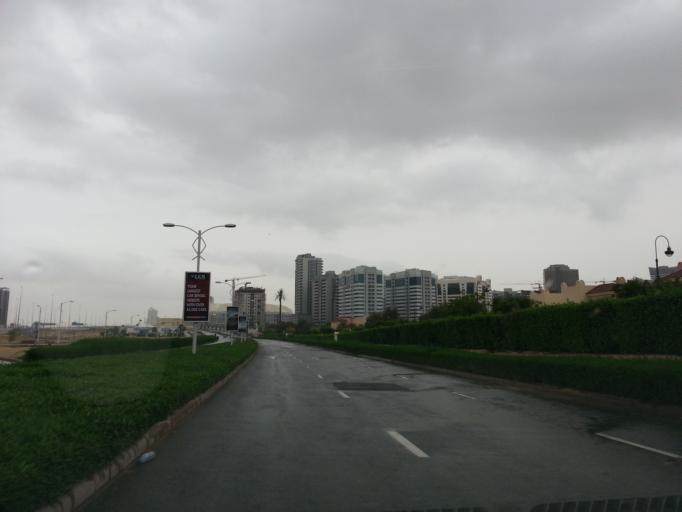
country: AE
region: Dubai
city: Dubai
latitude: 25.0433
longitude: 55.2085
